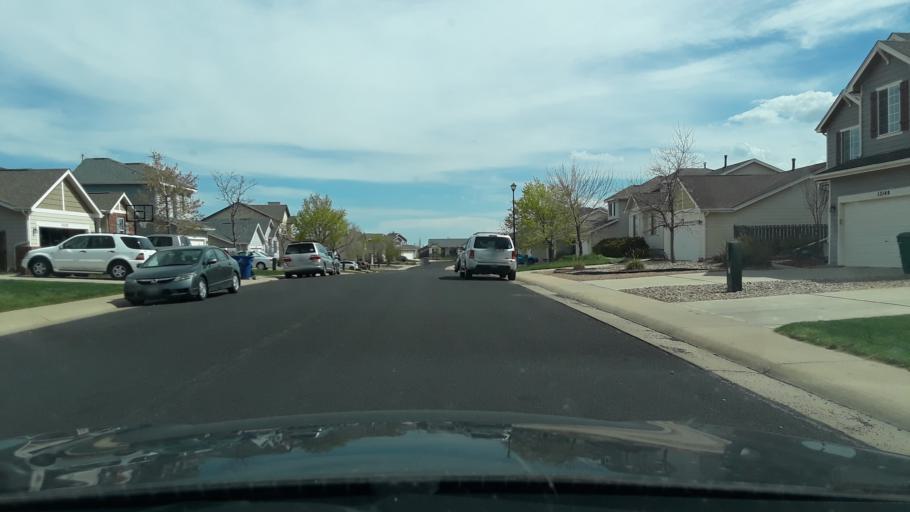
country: US
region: Colorado
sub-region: El Paso County
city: Monument
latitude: 39.0816
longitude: -104.8687
